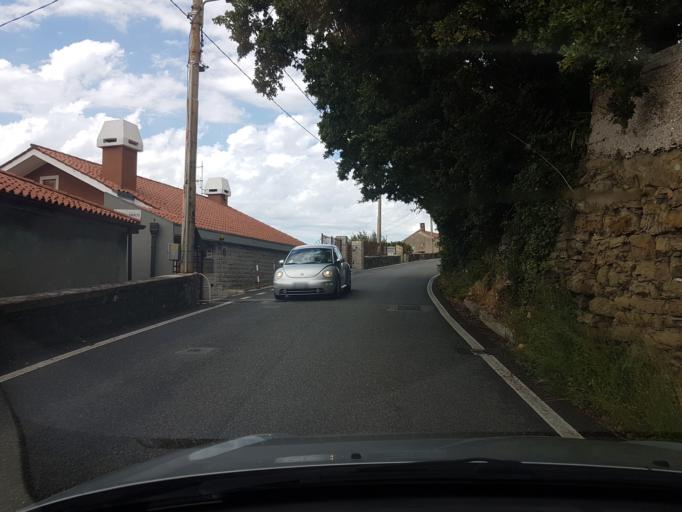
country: IT
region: Friuli Venezia Giulia
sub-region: Provincia di Trieste
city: Prosecco-Contovello
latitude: 45.6858
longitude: 13.7548
